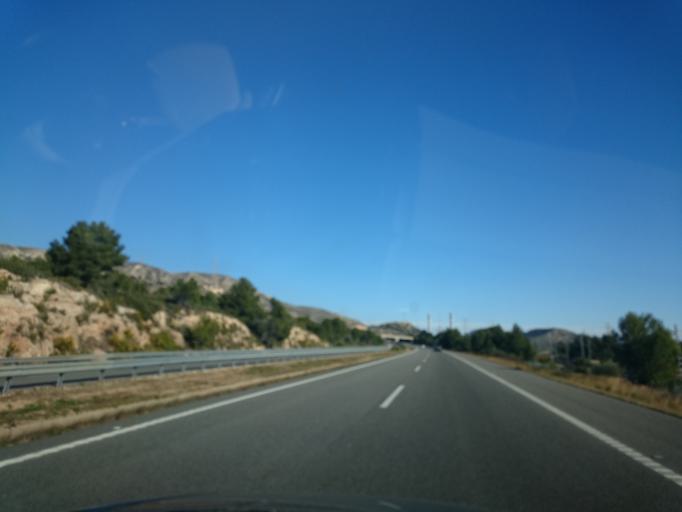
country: ES
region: Catalonia
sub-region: Provincia de Tarragona
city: l'Ametlla de Mar
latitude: 40.9481
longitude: 0.8591
